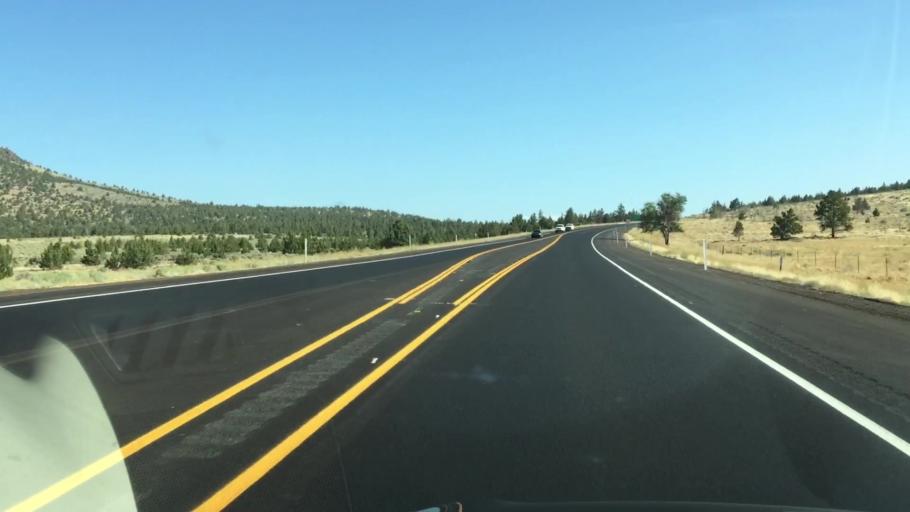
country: US
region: Oregon
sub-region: Jefferson County
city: Culver
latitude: 44.4635
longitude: -121.1990
